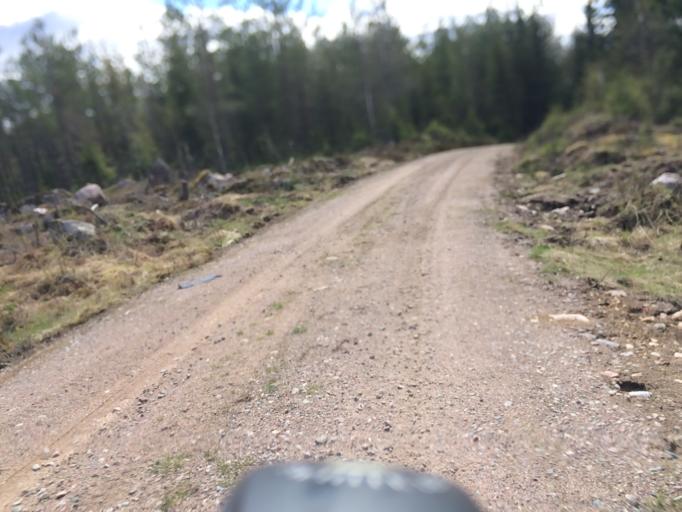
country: SE
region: OErebro
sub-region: Hallefors Kommun
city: Haellefors
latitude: 60.0491
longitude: 14.5164
